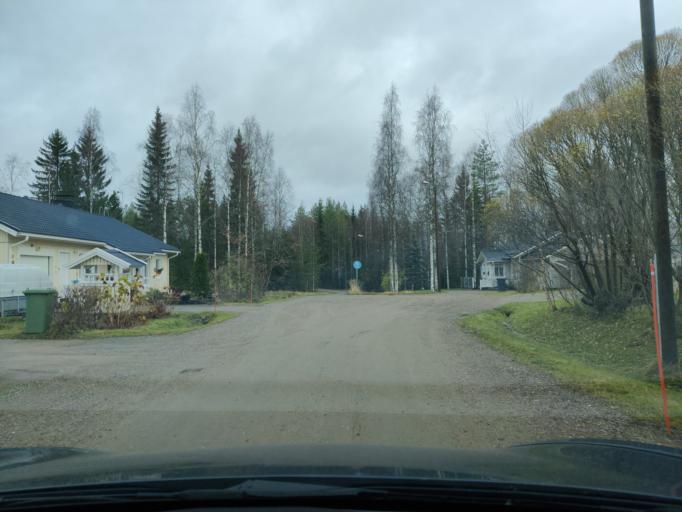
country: FI
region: Northern Savo
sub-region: Ylae-Savo
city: Kiuruvesi
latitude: 63.6404
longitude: 26.6414
